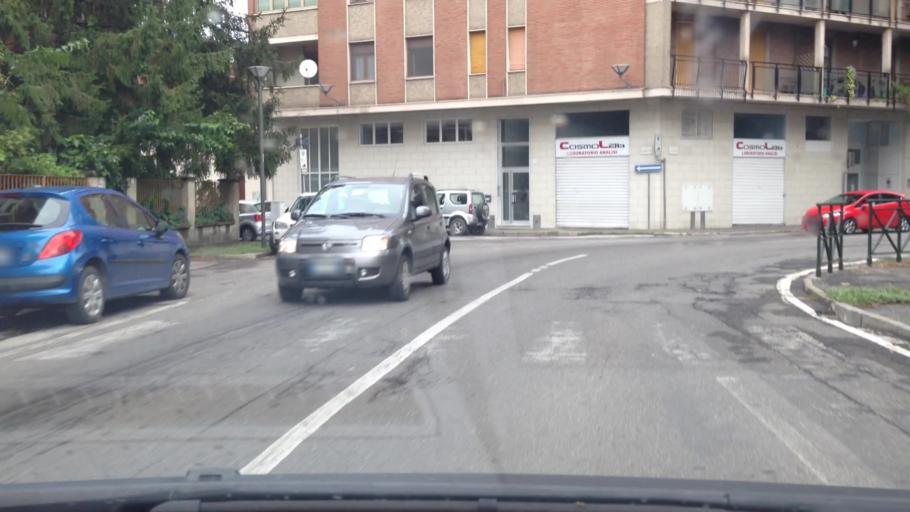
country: IT
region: Piedmont
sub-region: Provincia di Alessandria
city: Tortona
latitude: 44.8982
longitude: 8.8601
